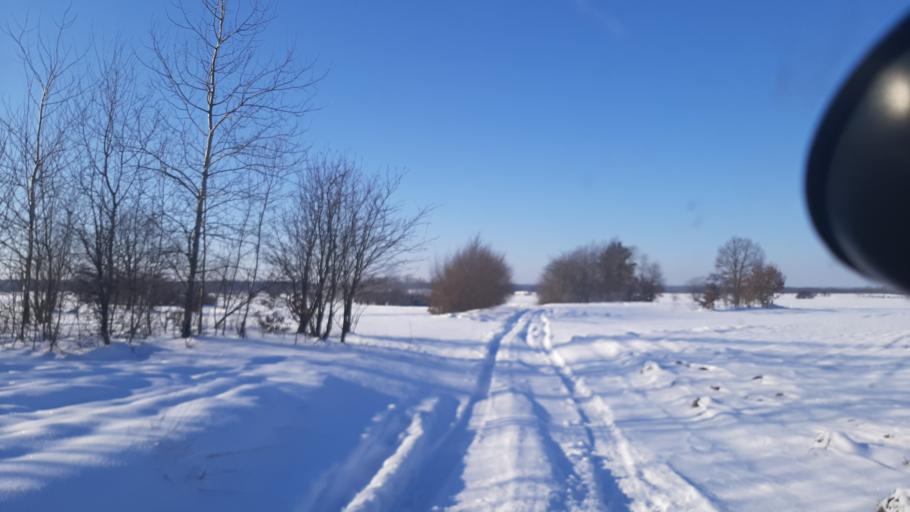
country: PL
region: Lublin Voivodeship
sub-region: Powiat lubelski
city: Jastkow
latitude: 51.3780
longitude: 22.4349
